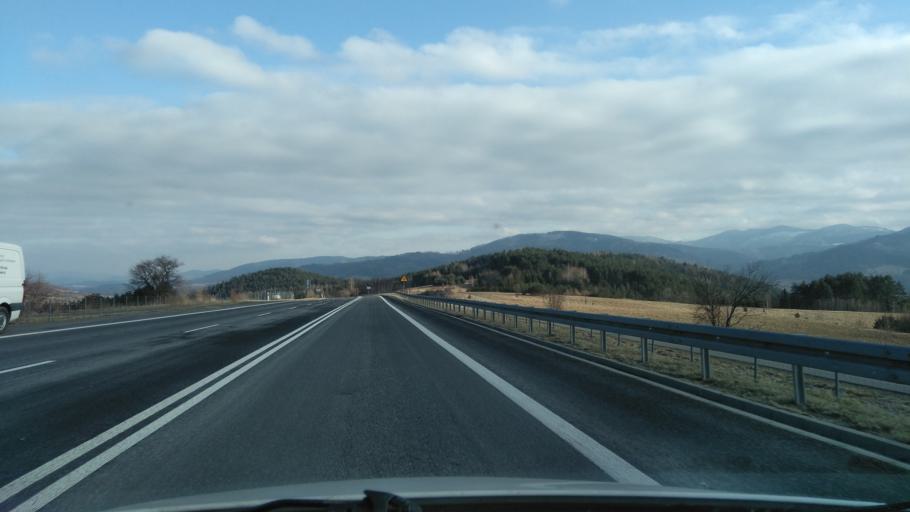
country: PL
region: Silesian Voivodeship
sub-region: Powiat zywiecki
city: Kamesznica
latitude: 49.5540
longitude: 19.0487
